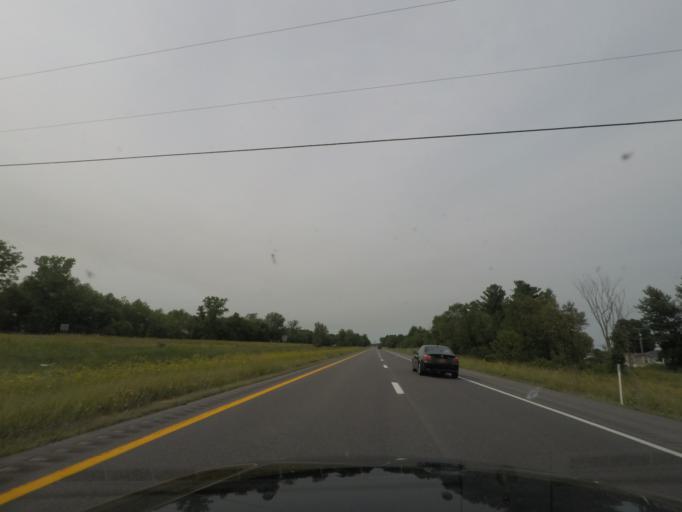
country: US
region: New York
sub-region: Clinton County
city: Cumberland Head
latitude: 44.8224
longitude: -73.4466
